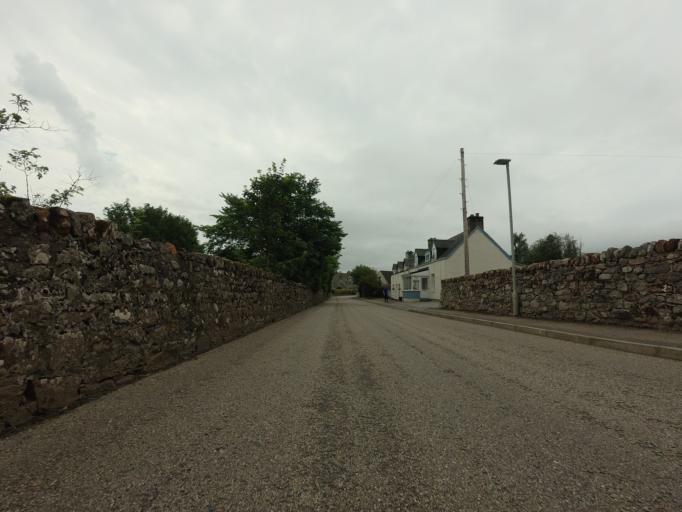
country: GB
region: Scotland
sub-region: Highland
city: Alness
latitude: 57.8833
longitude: -4.3645
